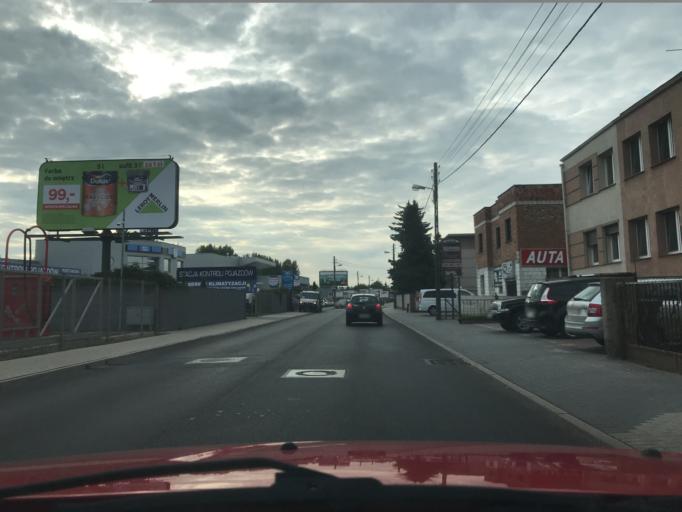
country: PL
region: Greater Poland Voivodeship
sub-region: Powiat poznanski
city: Plewiska
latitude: 52.3877
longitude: 16.8161
